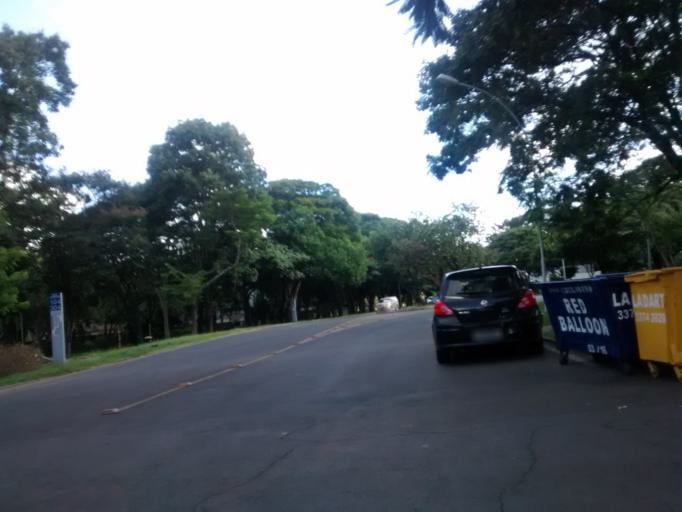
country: BR
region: Federal District
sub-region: Brasilia
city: Brasilia
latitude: -15.8079
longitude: -47.8958
